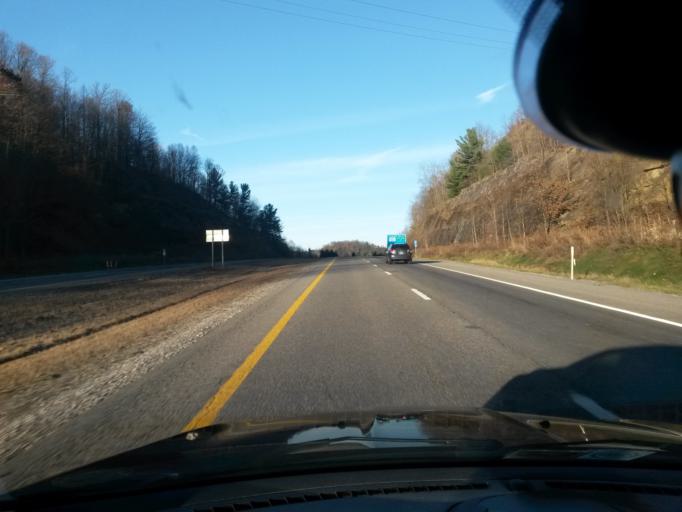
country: US
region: West Virginia
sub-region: Raleigh County
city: Prosperity
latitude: 37.8445
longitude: -81.2086
